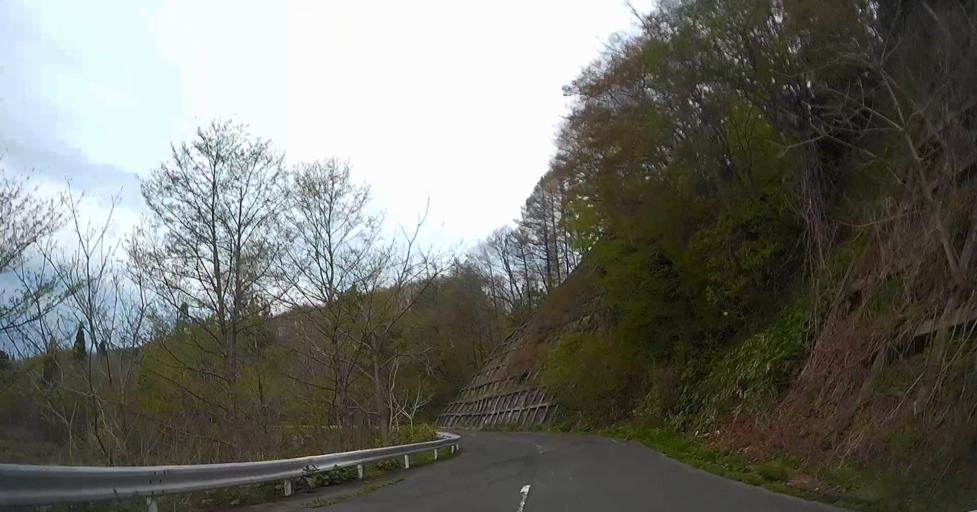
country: JP
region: Aomori
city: Goshogawara
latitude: 40.9035
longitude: 140.5257
